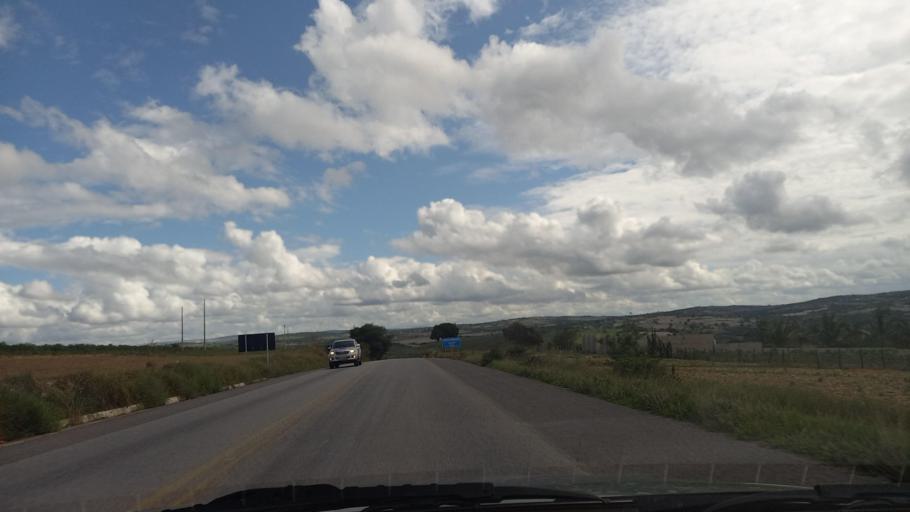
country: BR
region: Pernambuco
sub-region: Lajedo
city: Lajedo
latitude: -8.7232
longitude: -36.4278
